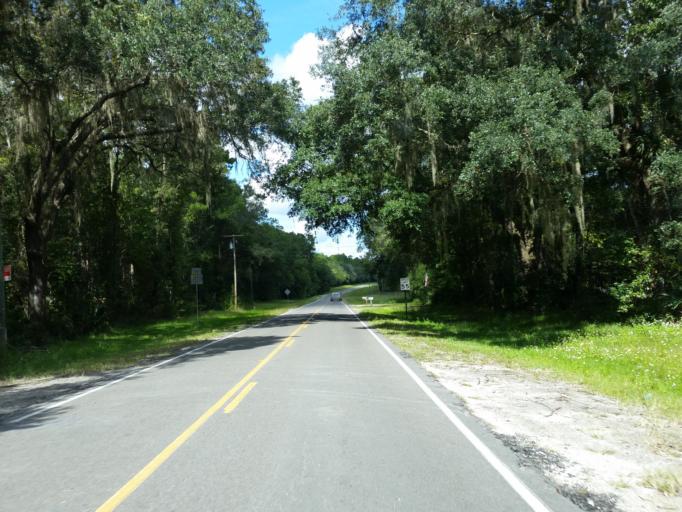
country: US
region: Florida
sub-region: Alachua County
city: Gainesville
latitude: 29.5126
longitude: -82.2795
